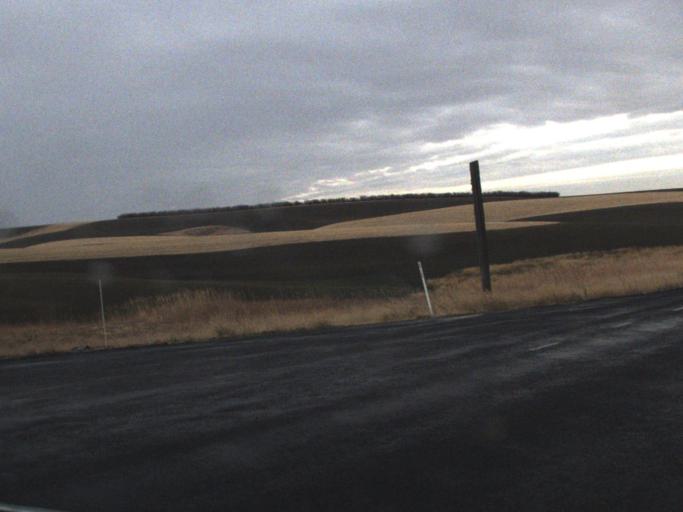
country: US
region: Washington
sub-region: Lincoln County
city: Davenport
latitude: 47.7218
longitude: -118.1520
